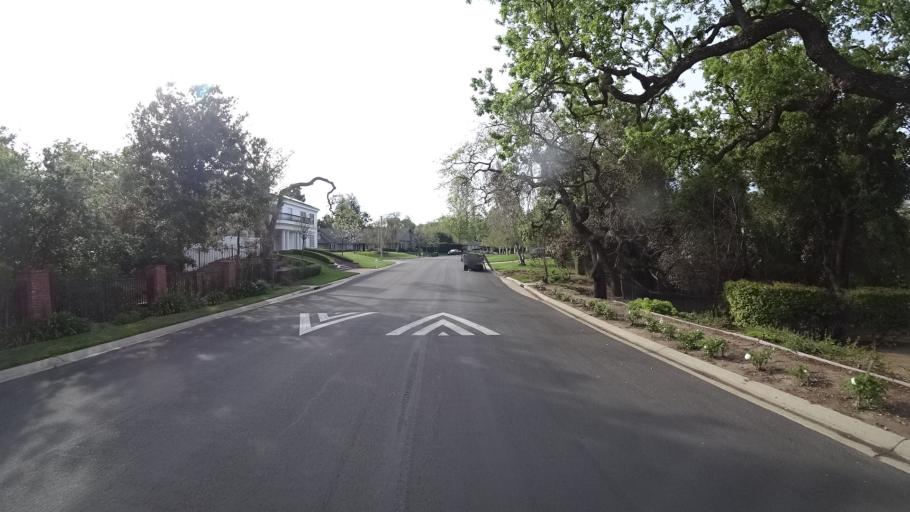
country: US
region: California
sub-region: Ventura County
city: Thousand Oaks
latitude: 34.1963
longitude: -118.8175
